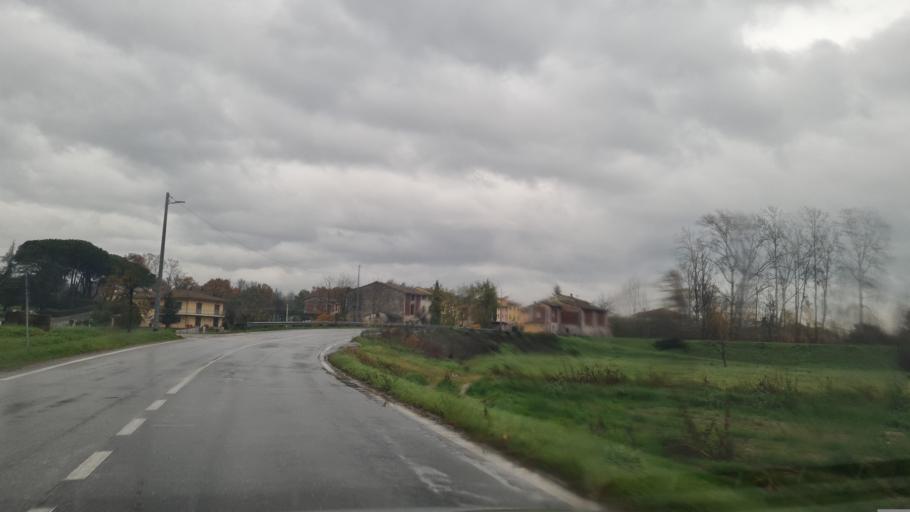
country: IT
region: Tuscany
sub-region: Provincia di Lucca
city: Lucca
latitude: 43.8626
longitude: 10.4692
